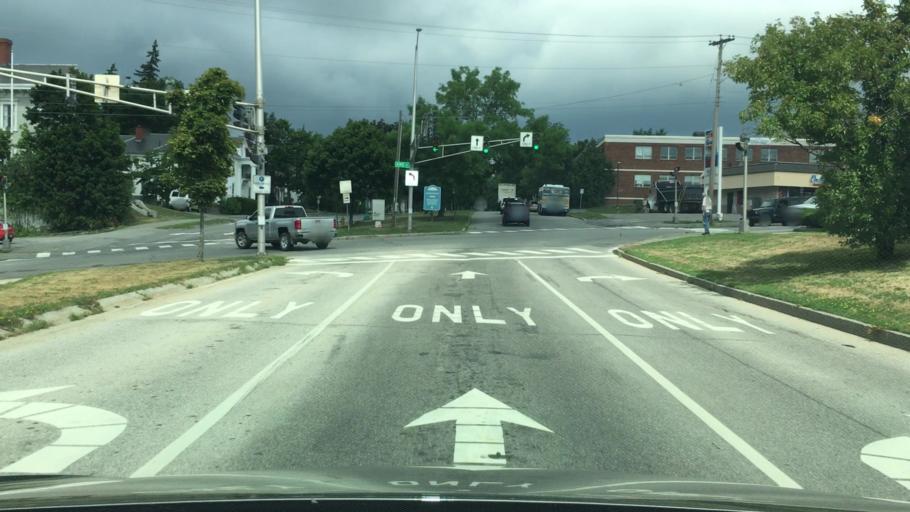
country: US
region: Maine
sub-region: Penobscot County
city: Brewer
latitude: 44.8028
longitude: -68.7673
